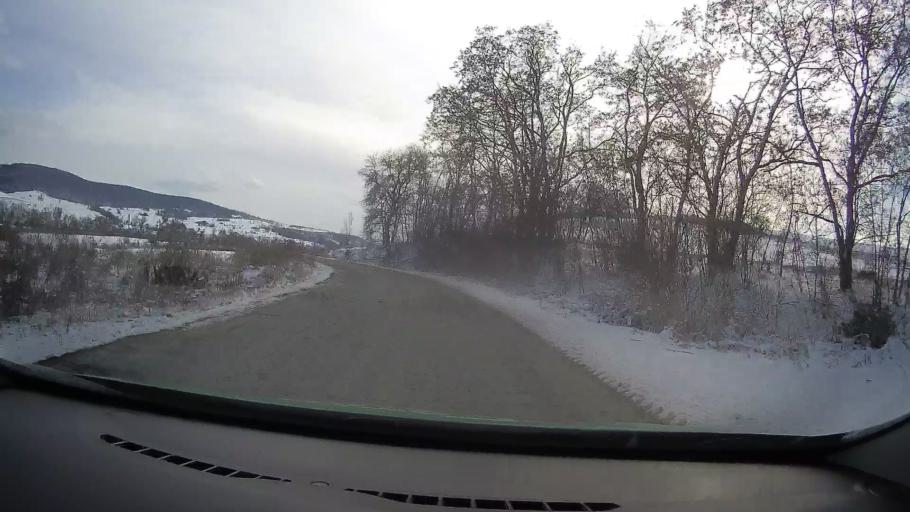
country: RO
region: Sibiu
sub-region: Comuna Iacobeni
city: Iacobeni
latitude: 46.0251
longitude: 24.7067
